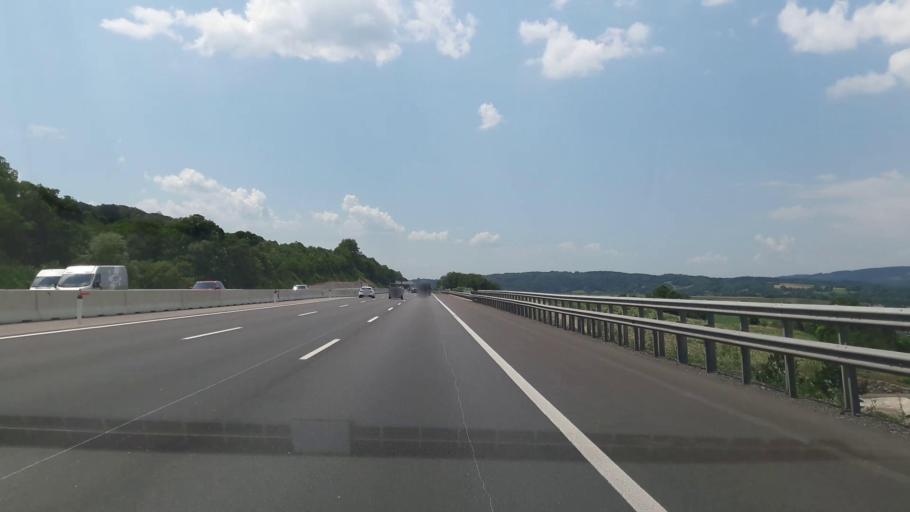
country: AT
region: Lower Austria
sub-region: Politischer Bezirk Melk
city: Klein-Poechlarn
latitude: 48.1961
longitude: 15.2238
